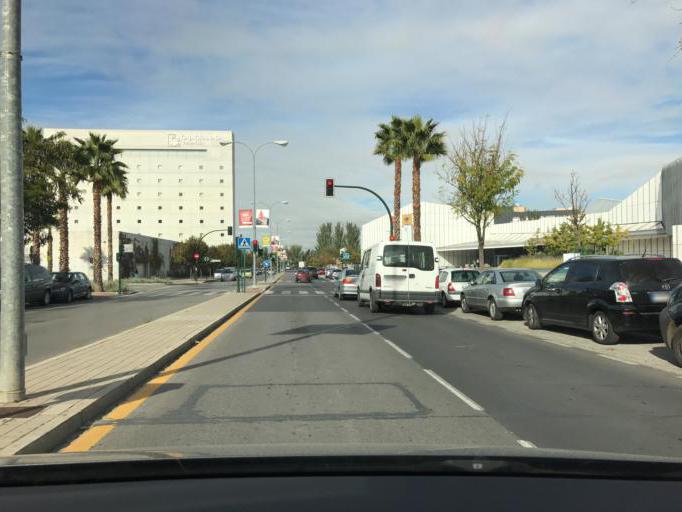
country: ES
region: Andalusia
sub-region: Provincia de Granada
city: Armilla
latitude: 37.1618
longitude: -3.6060
